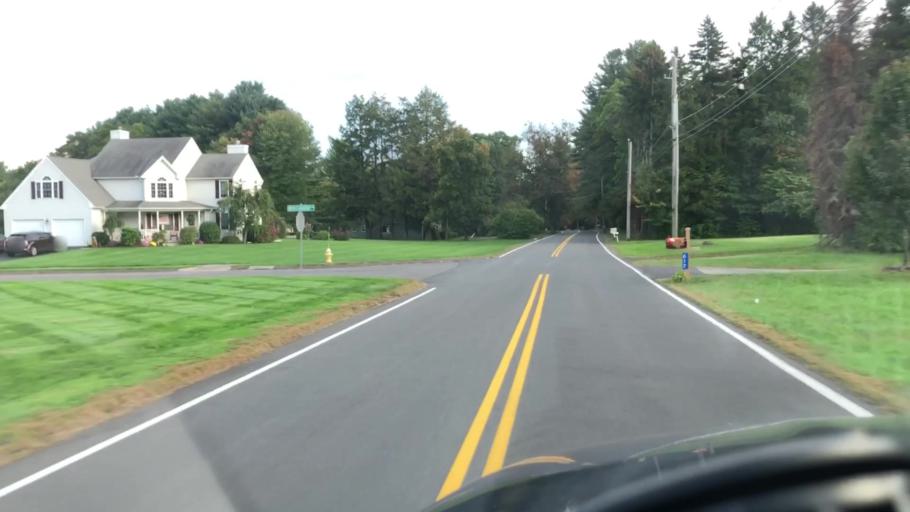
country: US
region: Connecticut
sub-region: Hartford County
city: Suffield Depot
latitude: 42.0213
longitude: -72.6610
